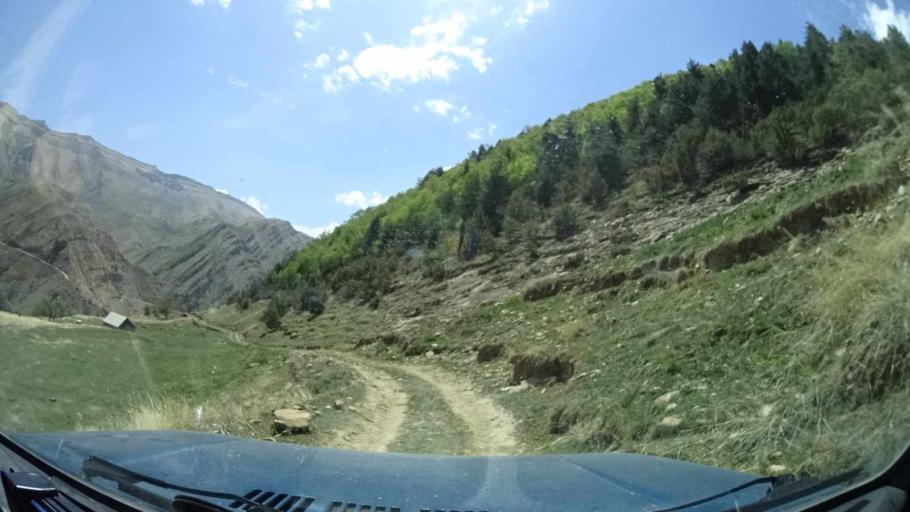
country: RU
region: Dagestan
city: Gunib
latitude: 42.3081
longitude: 47.0017
